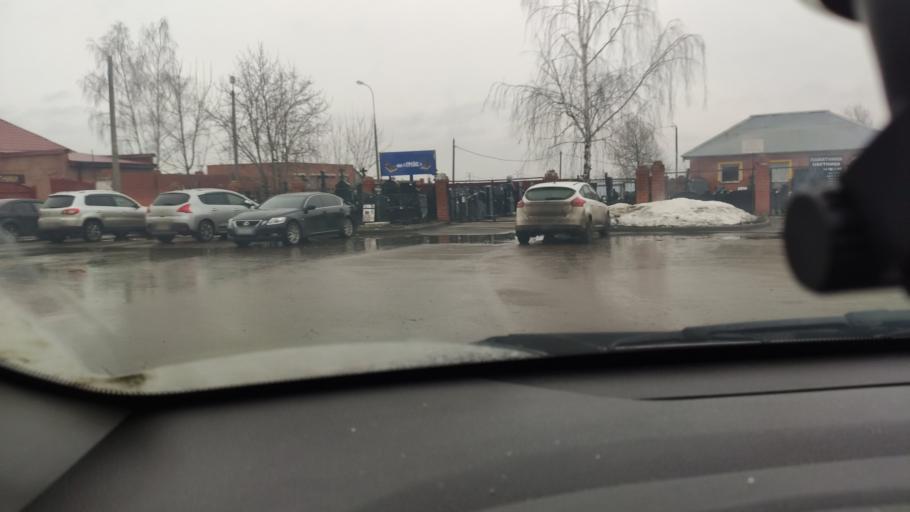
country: RU
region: Moskovskaya
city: Yakovlevskoye
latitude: 55.4532
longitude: 37.8938
